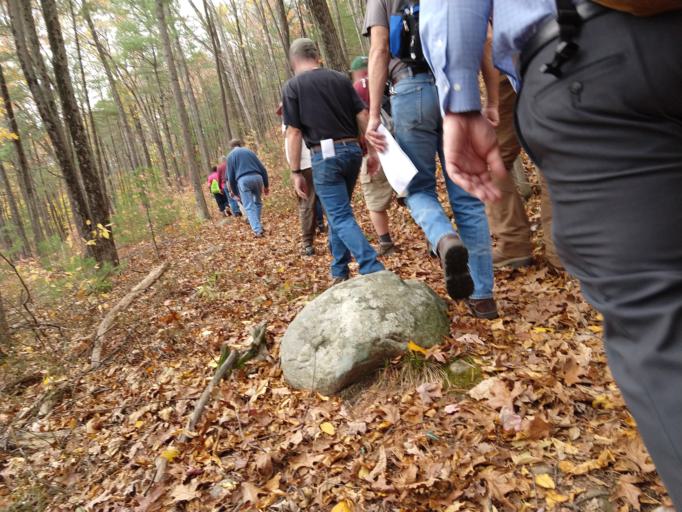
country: US
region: Massachusetts
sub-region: Worcester County
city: Leominster
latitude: 42.5226
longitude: -71.7720
